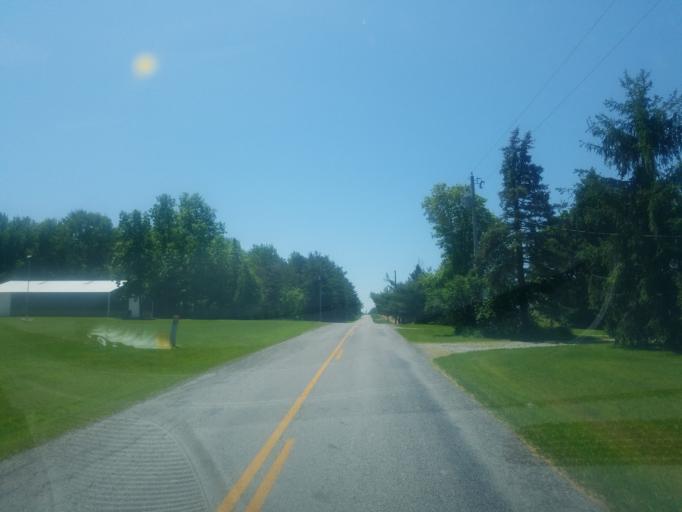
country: US
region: Ohio
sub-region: Huron County
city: New London
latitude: 41.1447
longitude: -82.3794
